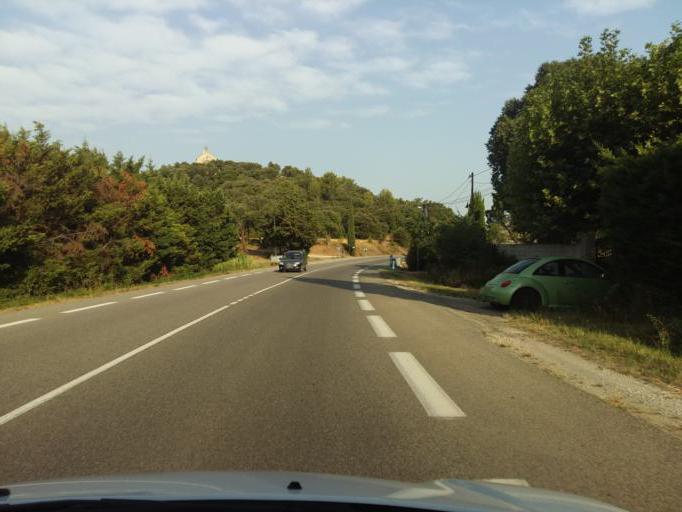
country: FR
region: Provence-Alpes-Cote d'Azur
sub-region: Departement du Vaucluse
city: Bollene
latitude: 44.2749
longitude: 4.7912
